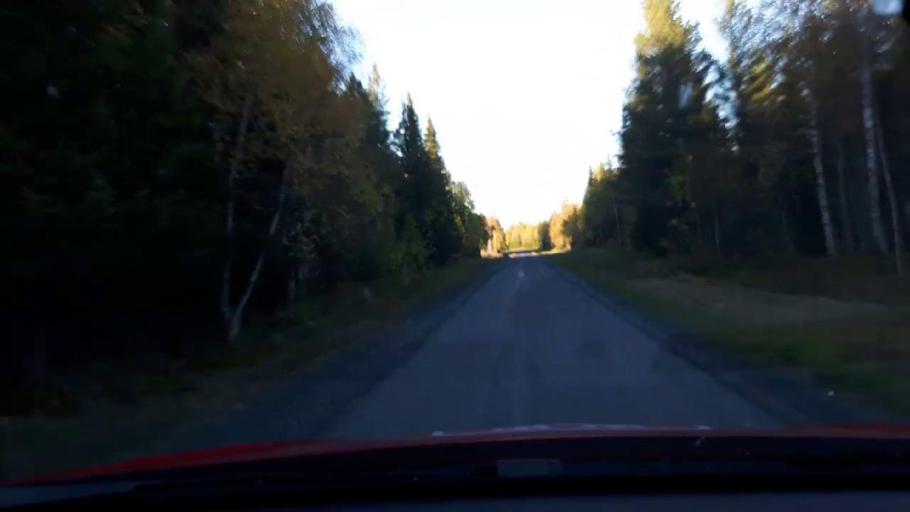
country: SE
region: Jaemtland
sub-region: Krokoms Kommun
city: Krokom
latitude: 63.4255
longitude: 14.6093
